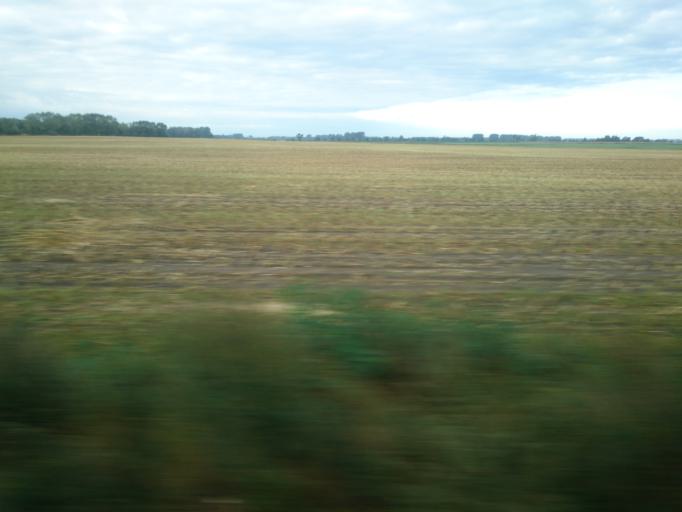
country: DE
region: Mecklenburg-Vorpommern
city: Ferdinandshof
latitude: 53.6729
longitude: 13.8864
